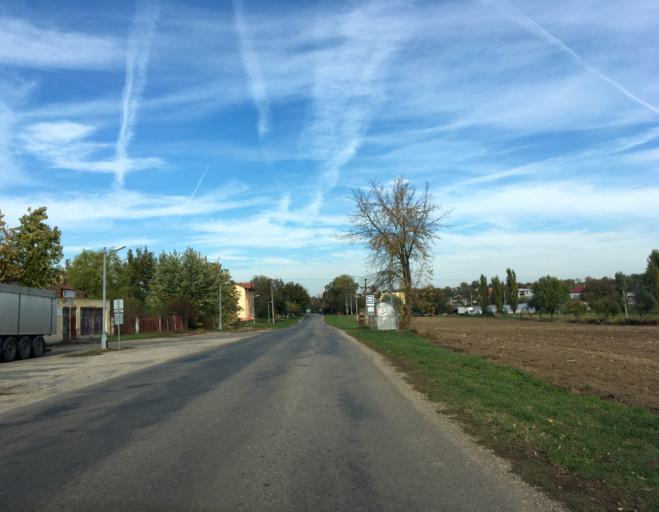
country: SK
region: Nitriansky
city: Svodin
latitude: 47.9826
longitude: 18.4017
